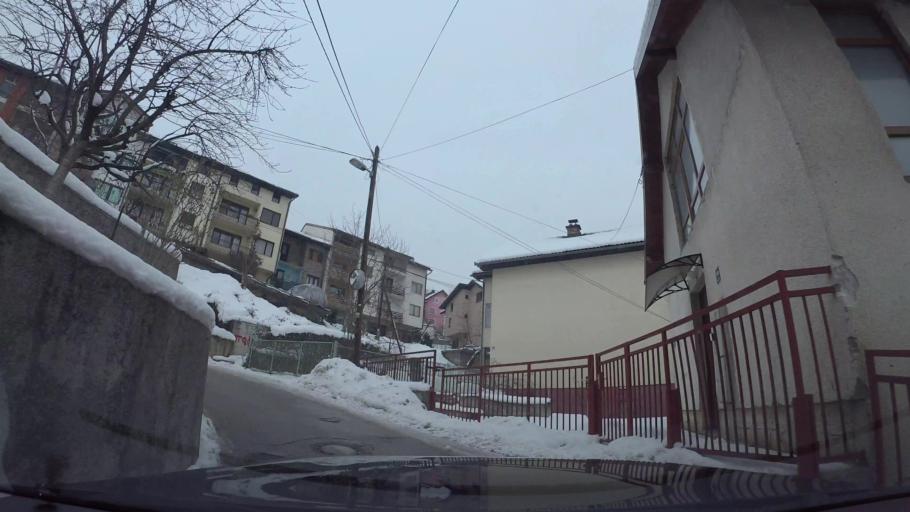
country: BA
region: Federation of Bosnia and Herzegovina
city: Kobilja Glava
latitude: 43.8644
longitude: 18.3892
